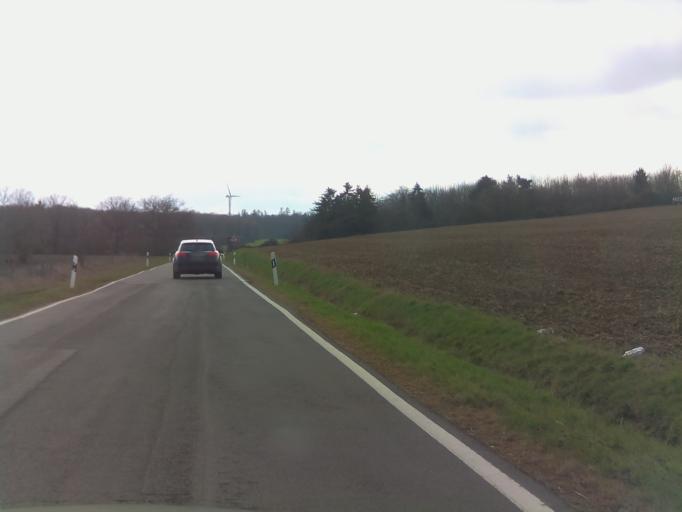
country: DE
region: Rheinland-Pfalz
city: Morsfeld
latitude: 49.7650
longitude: 7.9388
